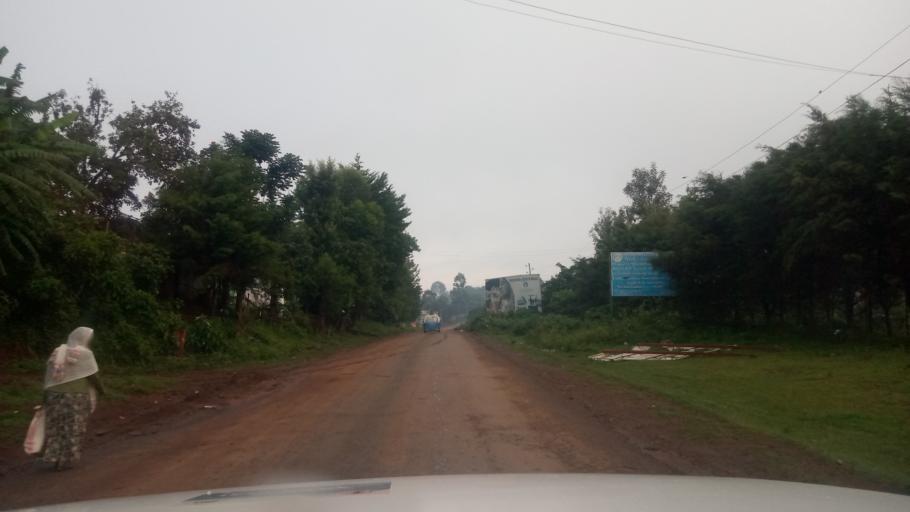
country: ET
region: Oromiya
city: Jima
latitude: 7.6934
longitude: 36.8211
